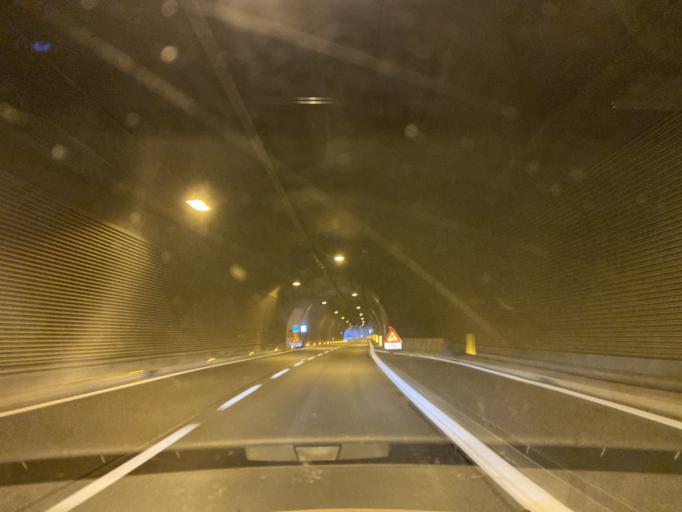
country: IT
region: Piedmont
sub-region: Provincia di Torino
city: Susa
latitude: 45.1428
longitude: 7.0619
